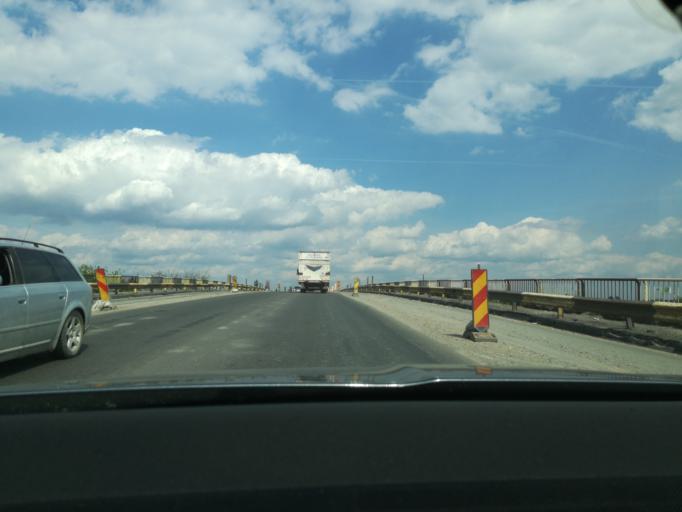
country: RO
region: Ilfov
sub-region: Comuna Chitila
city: Chitila
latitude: 44.4959
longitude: 25.9926
